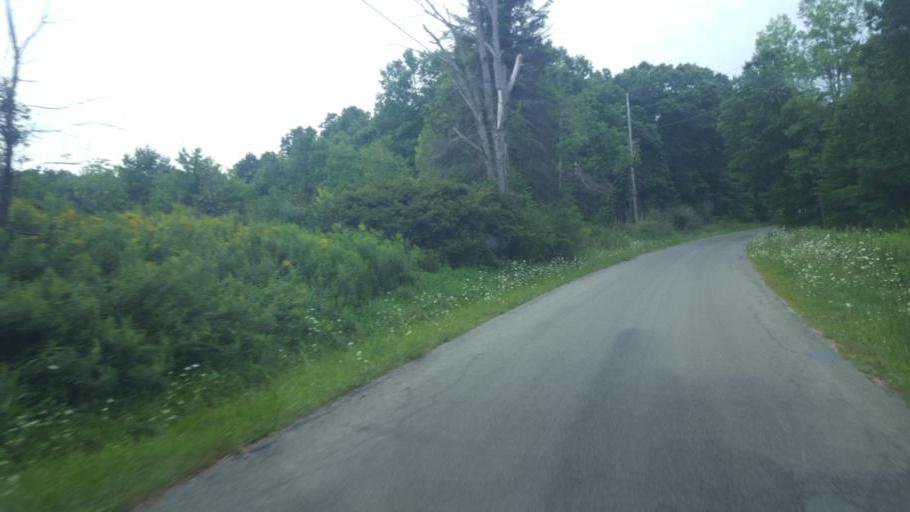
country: US
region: Pennsylvania
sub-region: Clarion County
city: Marianne
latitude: 41.2134
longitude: -79.4258
